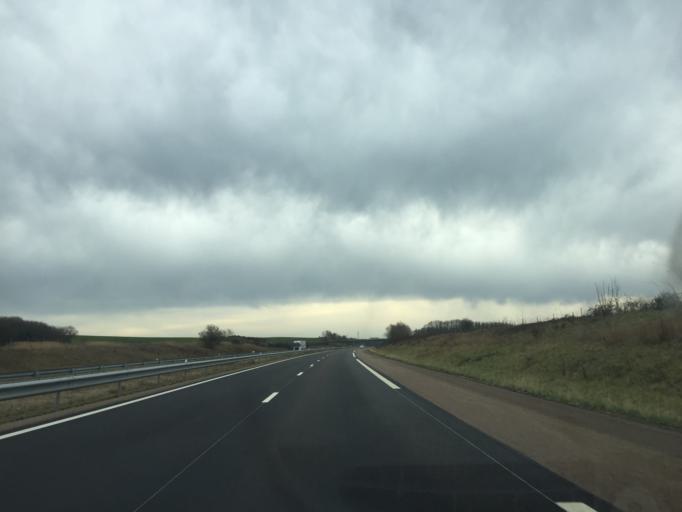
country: FR
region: Franche-Comte
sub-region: Departement du Jura
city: Bletterans
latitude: 46.7408
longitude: 5.5109
